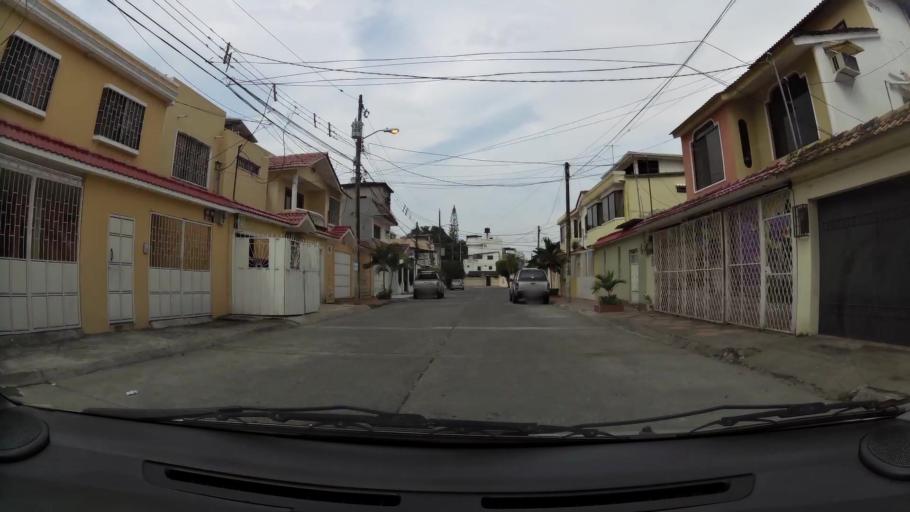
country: EC
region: Guayas
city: Eloy Alfaro
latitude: -2.1150
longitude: -79.8904
